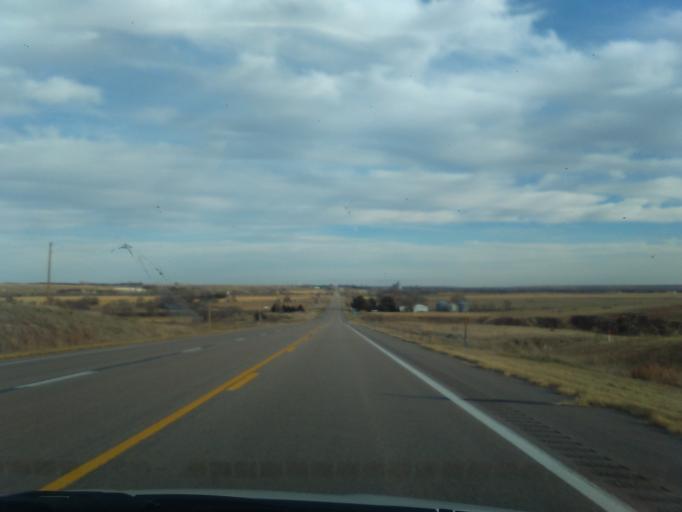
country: US
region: Nebraska
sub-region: Hitchcock County
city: Trenton
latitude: 40.2343
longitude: -100.9023
